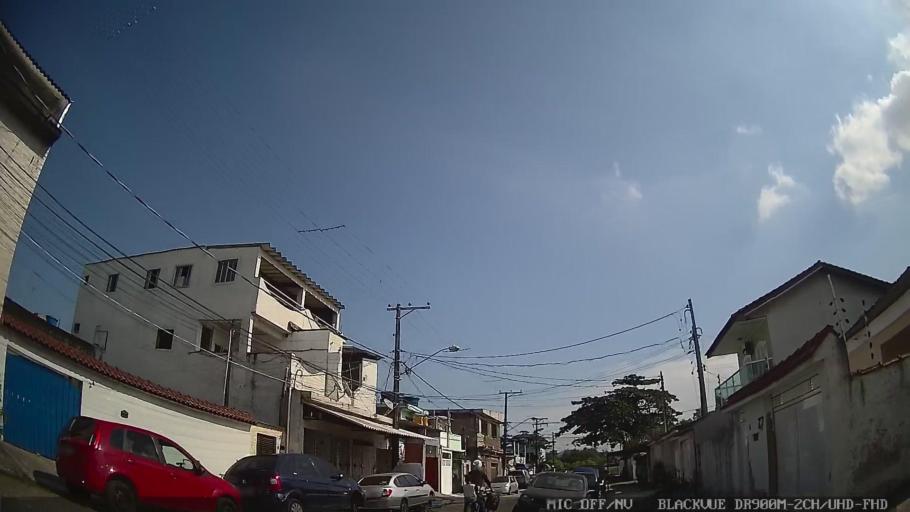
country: BR
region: Sao Paulo
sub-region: Santos
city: Santos
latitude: -23.9440
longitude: -46.3054
